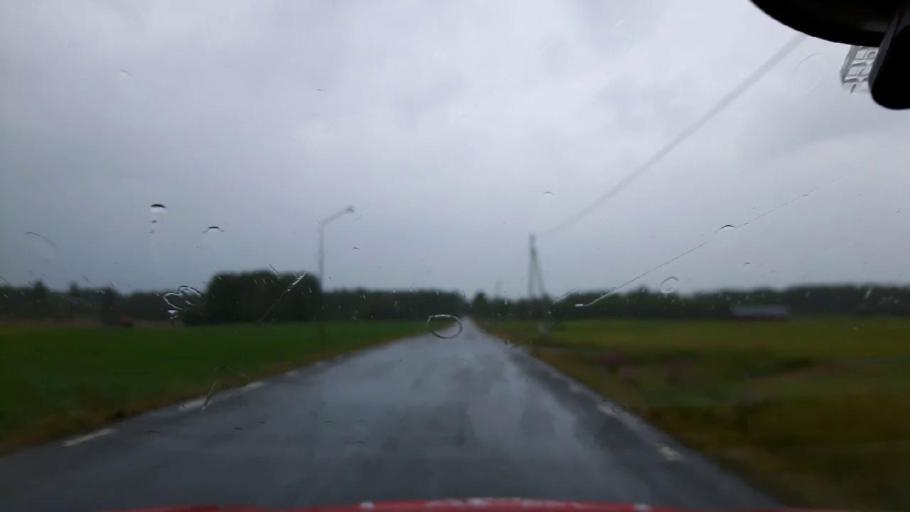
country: SE
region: Jaemtland
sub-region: OEstersunds Kommun
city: Brunflo
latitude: 62.9928
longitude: 14.7905
